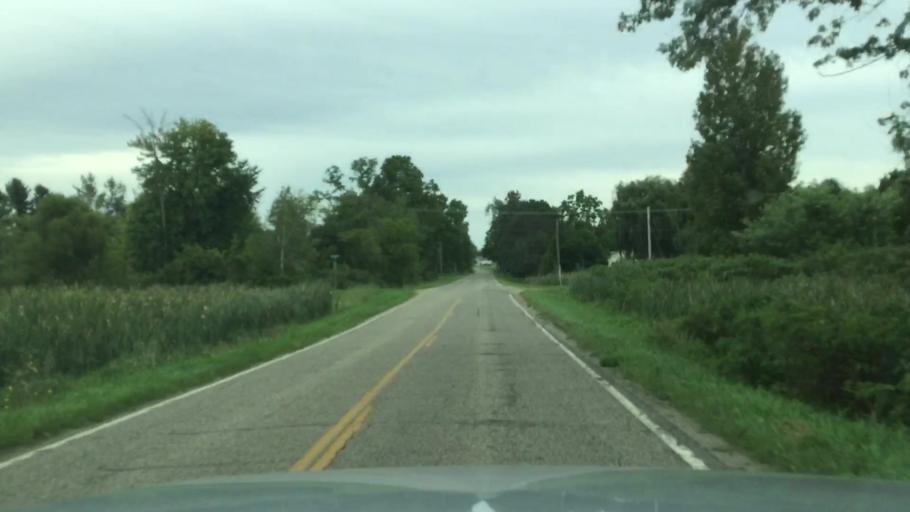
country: US
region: Michigan
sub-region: Shiawassee County
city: Durand
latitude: 42.8885
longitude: -84.0690
